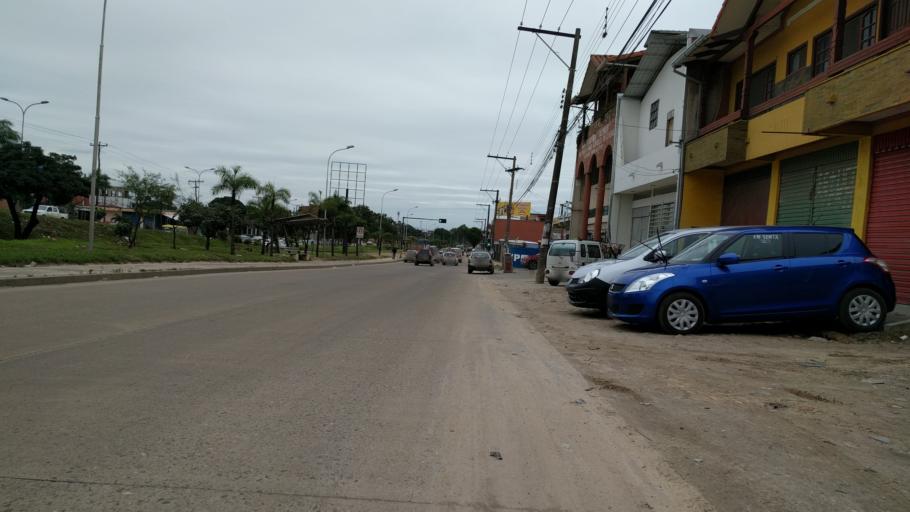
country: BO
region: Santa Cruz
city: Santa Cruz de la Sierra
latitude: -17.8172
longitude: -63.2012
